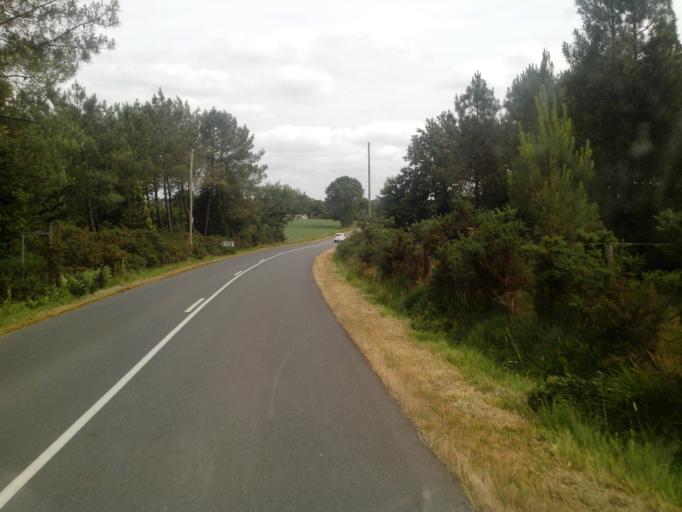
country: FR
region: Brittany
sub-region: Departement d'Ille-et-Vilaine
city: Plelan-le-Grand
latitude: 48.0072
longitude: -2.1218
